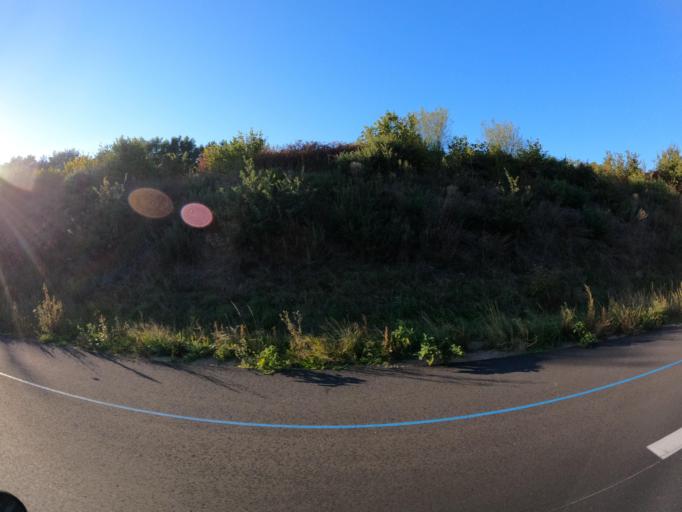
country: FR
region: Pays de la Loire
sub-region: Departement de la Vendee
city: Beaurepaire
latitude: 46.8900
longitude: -1.0978
